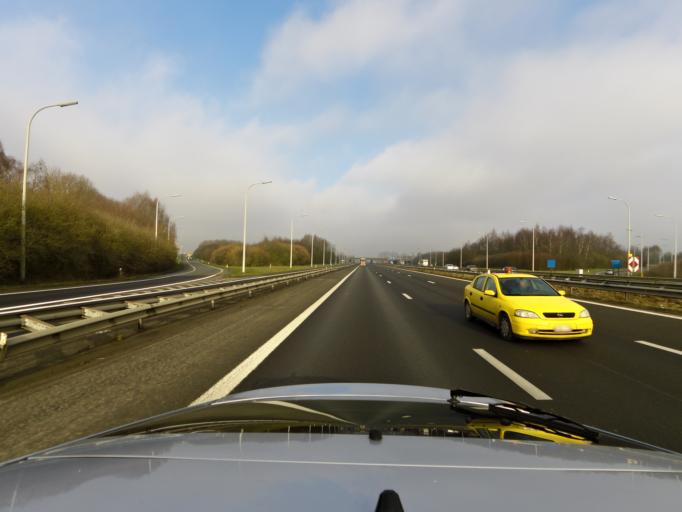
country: BE
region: Flanders
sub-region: Provincie West-Vlaanderen
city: Wevelgem
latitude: 50.8261
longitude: 3.1913
